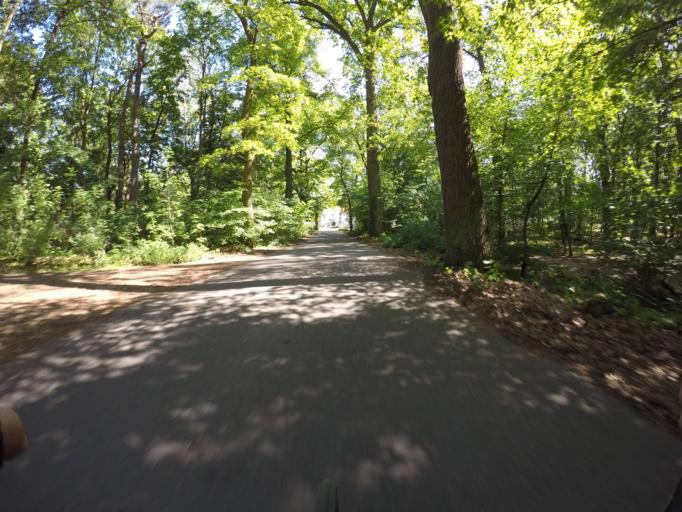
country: DE
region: Berlin
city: Wannsee
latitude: 52.4199
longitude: 13.1520
